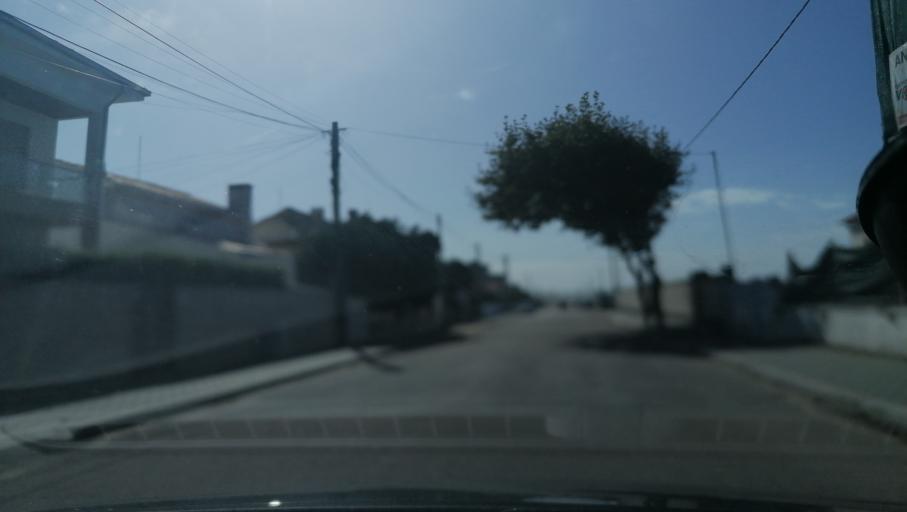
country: PT
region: Porto
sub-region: Vila Nova de Gaia
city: Arcozelo
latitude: 41.0372
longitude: -8.6477
